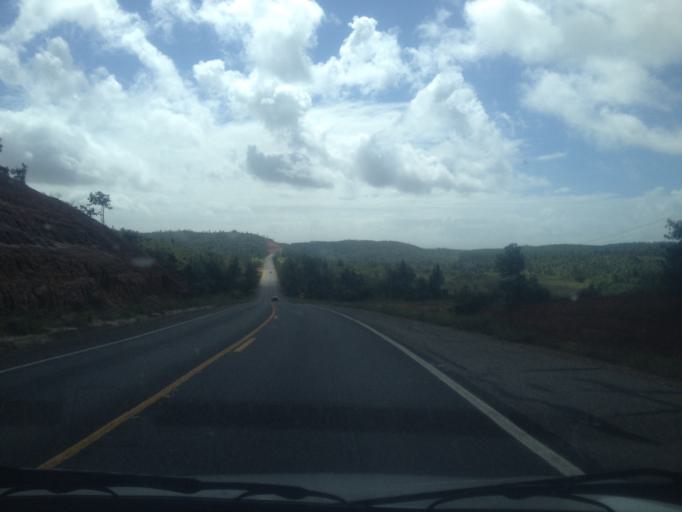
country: BR
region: Bahia
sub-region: Conde
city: Conde
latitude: -11.9937
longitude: -37.6788
